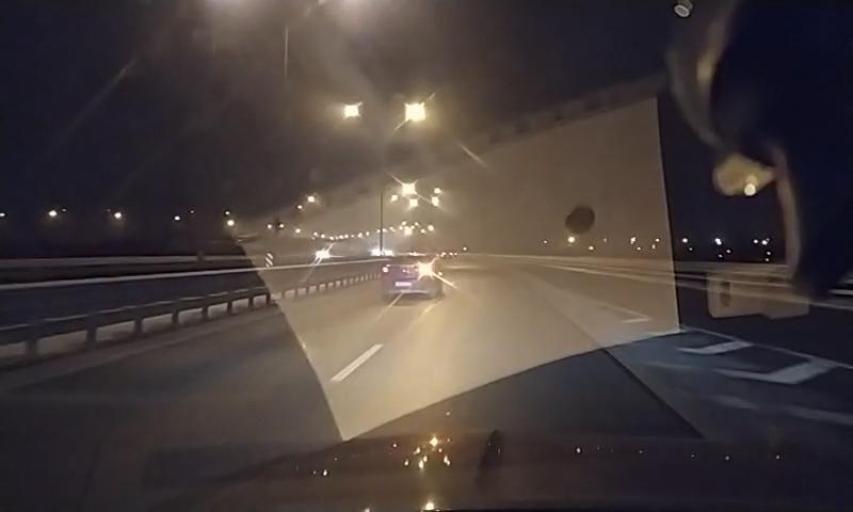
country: RU
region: Leningrad
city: Bugry
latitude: 60.0978
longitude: 30.3815
